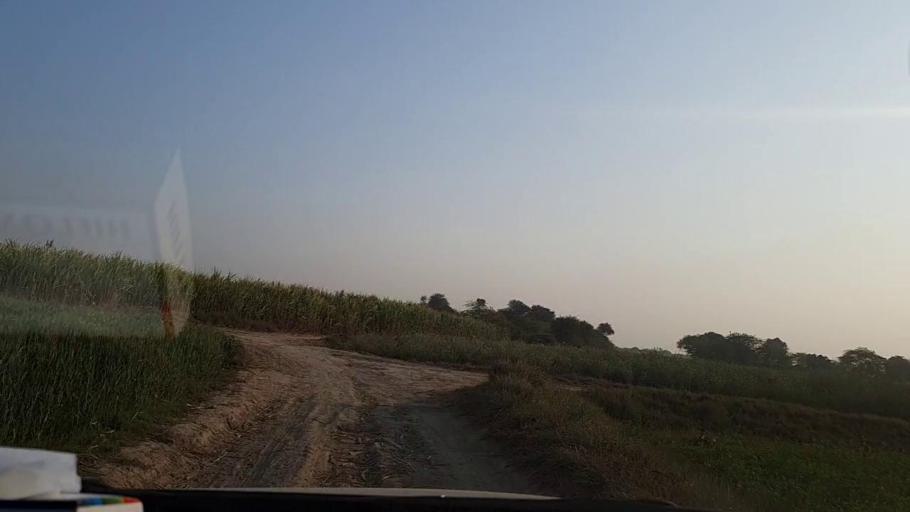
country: PK
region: Sindh
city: Tando Ghulam Ali
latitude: 25.2046
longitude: 68.9216
